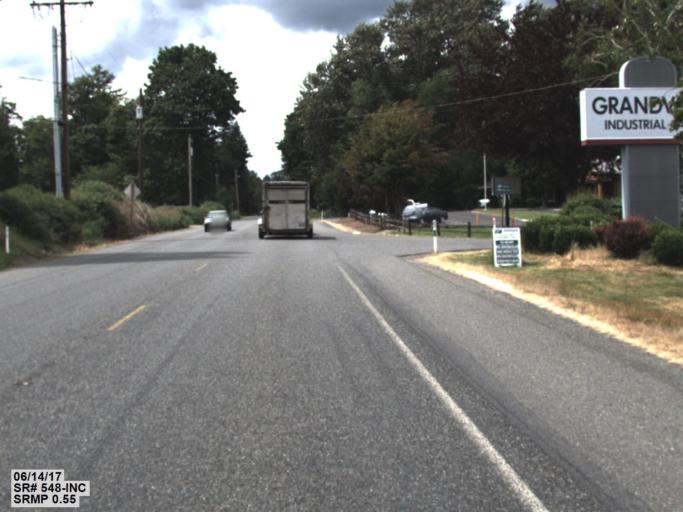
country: US
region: Washington
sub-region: Whatcom County
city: Ferndale
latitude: 48.8920
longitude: -122.6082
